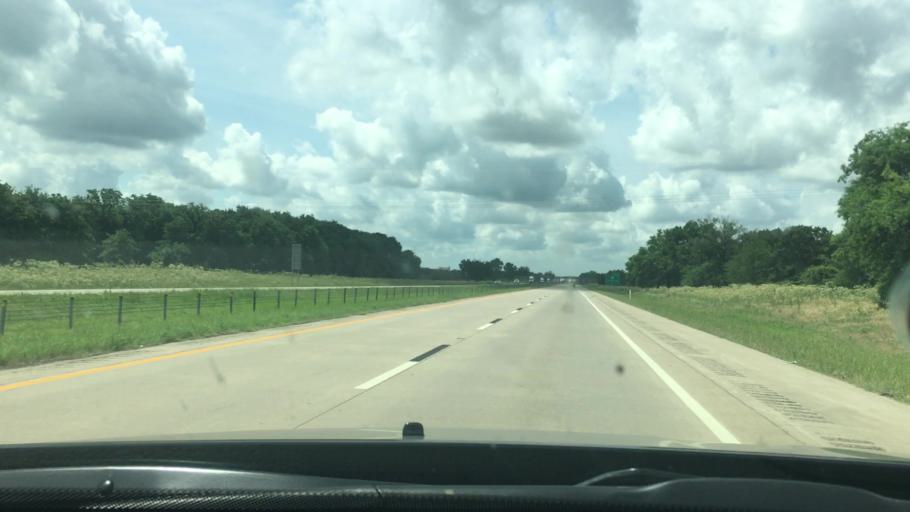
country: US
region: Oklahoma
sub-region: Love County
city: Marietta
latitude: 33.8034
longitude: -97.1351
